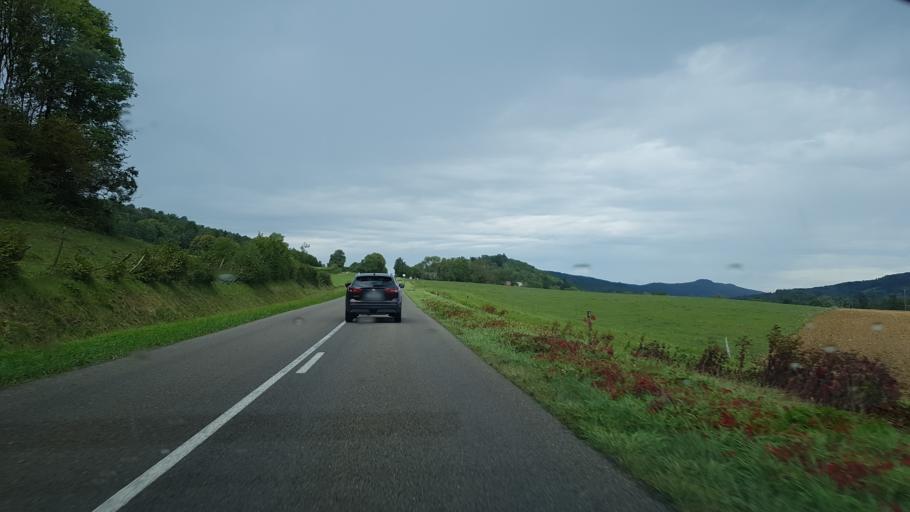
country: FR
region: Rhone-Alpes
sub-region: Departement de l'Ain
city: Cuisiat
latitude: 46.3219
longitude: 5.4421
